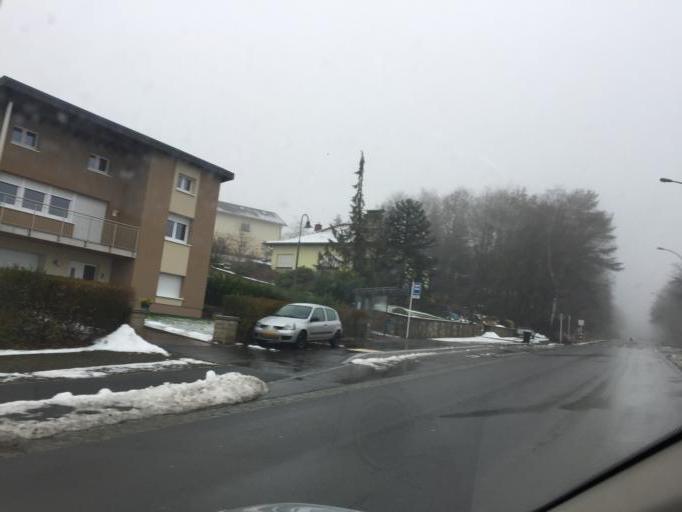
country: LU
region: Diekirch
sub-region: Canton de Diekirch
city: Niederfeulen
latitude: 49.8573
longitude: 6.0388
